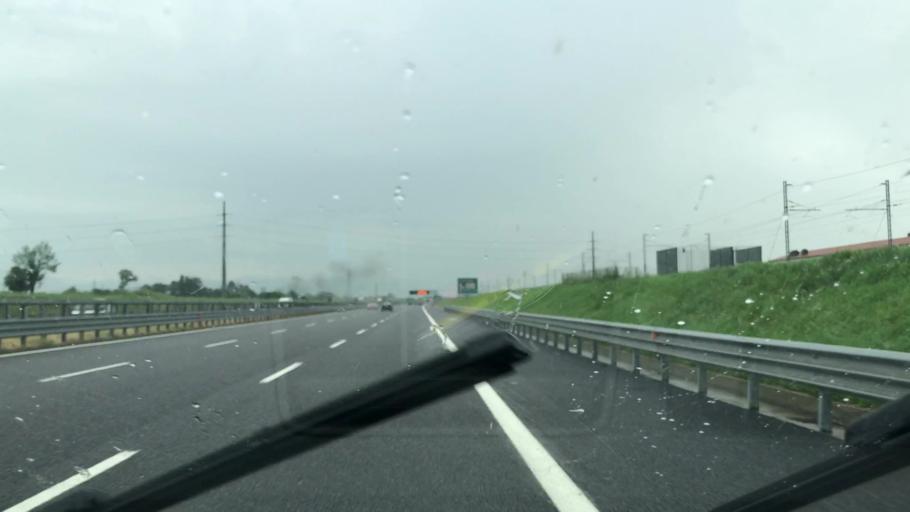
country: IT
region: Lombardy
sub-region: Provincia di Brescia
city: Rudiano
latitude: 45.5112
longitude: 9.9047
